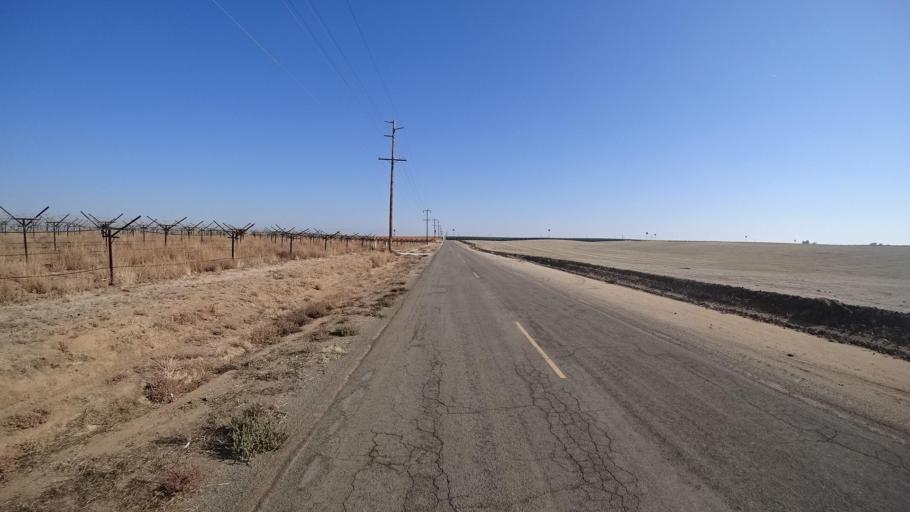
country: US
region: California
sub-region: Kern County
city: McFarland
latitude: 35.7035
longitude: -119.1408
